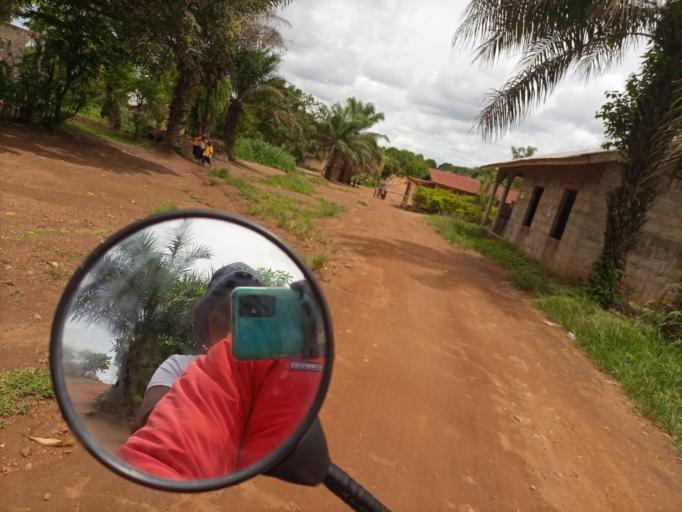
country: SL
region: Southern Province
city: Baoma
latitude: 7.9705
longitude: -11.7151
